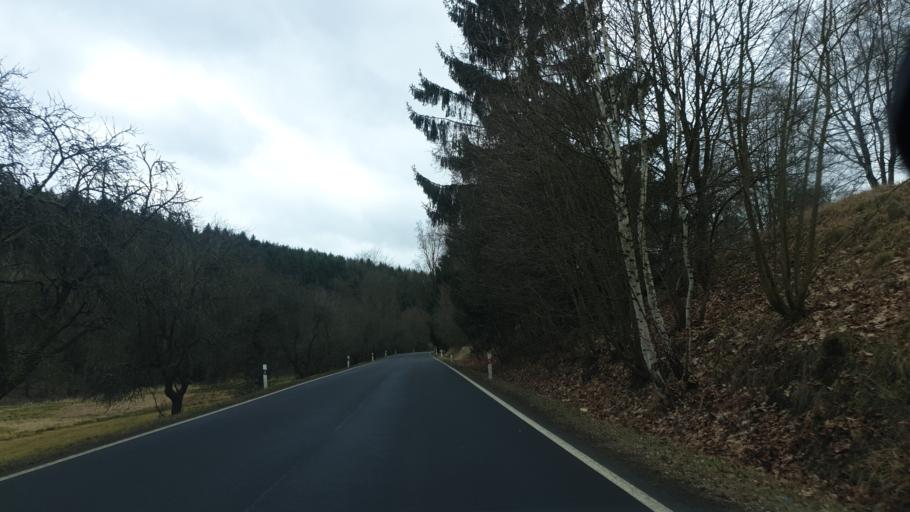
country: CZ
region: Karlovarsky
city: As
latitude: 50.2426
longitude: 12.1907
